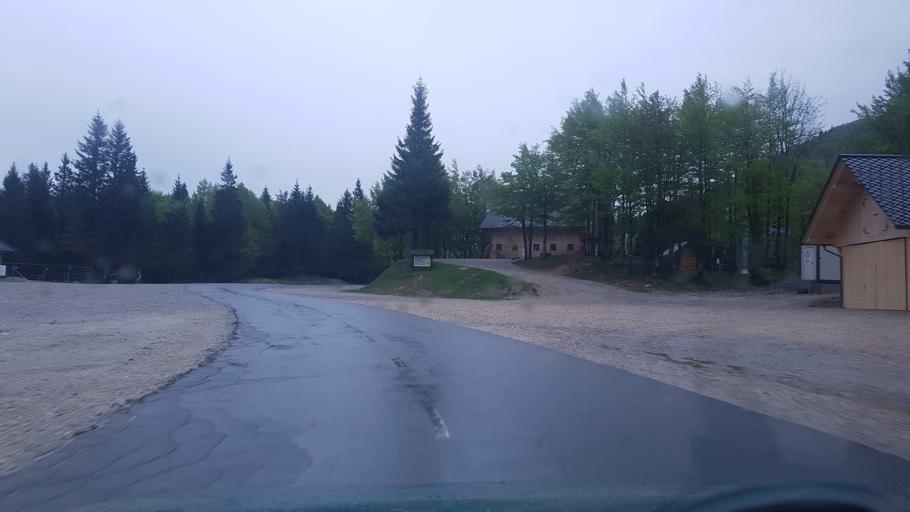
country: SI
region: Bohinj
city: Bohinjska Bistrica
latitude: 46.2418
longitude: 14.0086
